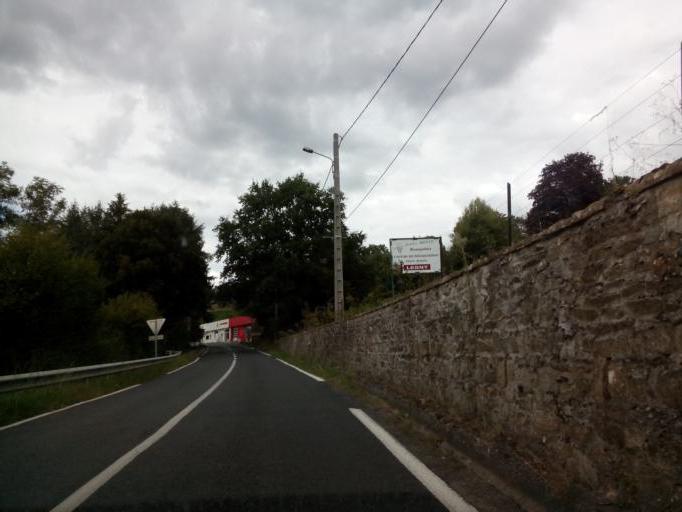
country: FR
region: Rhone-Alpes
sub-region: Departement du Rhone
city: Saint-Verand
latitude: 45.9087
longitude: 4.5735
